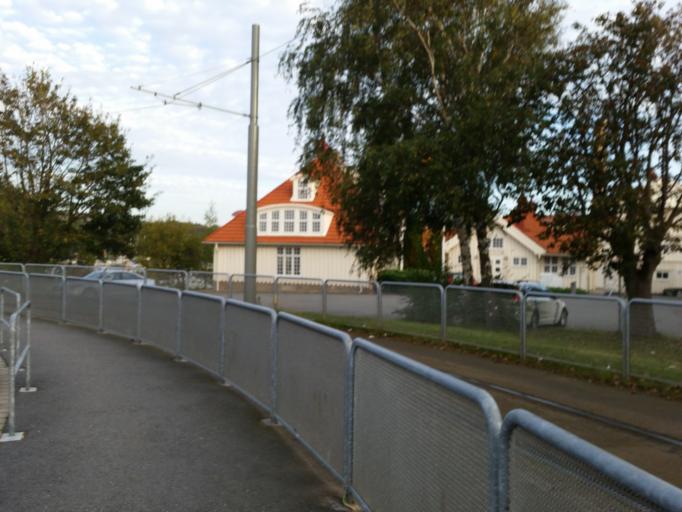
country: SE
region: Vaestra Goetaland
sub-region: Goteborg
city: Styrso
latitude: 57.6604
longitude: 11.8458
